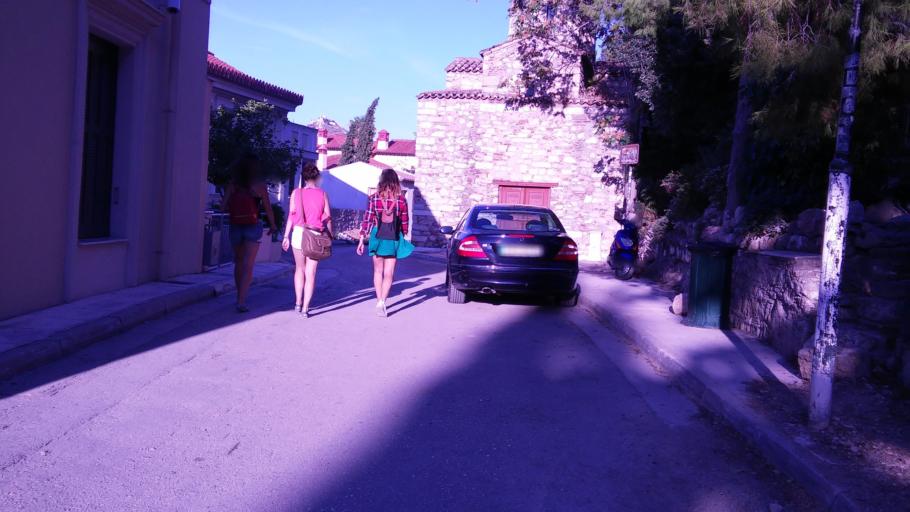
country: GR
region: Attica
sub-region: Nomarchia Athinas
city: Athens
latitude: 37.9728
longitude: 23.7263
